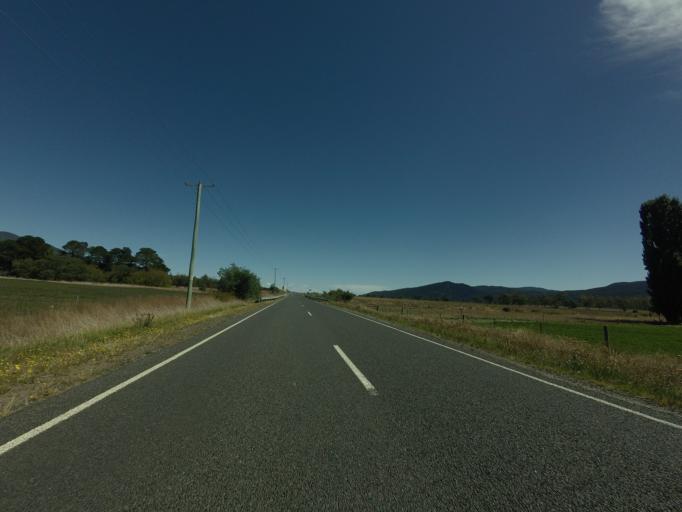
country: AU
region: Tasmania
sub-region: Break O'Day
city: St Helens
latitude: -41.7099
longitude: 147.8430
